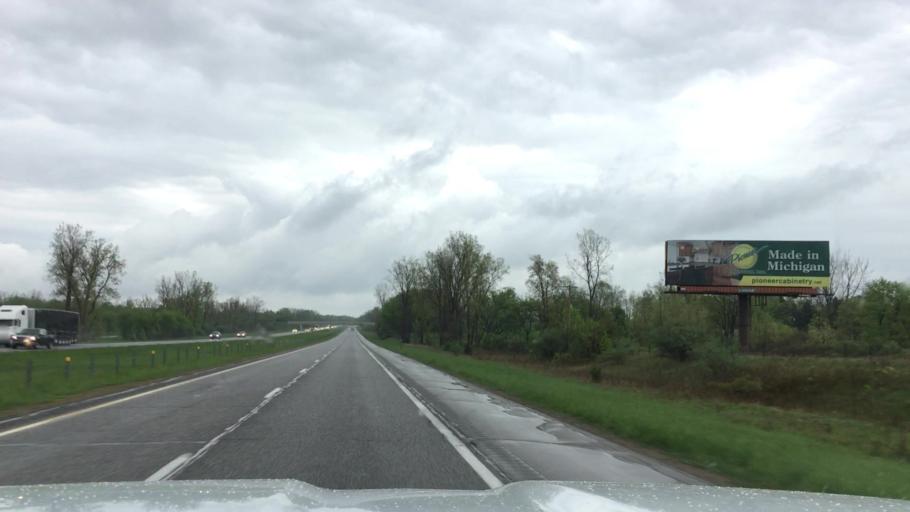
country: US
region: Michigan
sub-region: Shiawassee County
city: Perry
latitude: 42.8481
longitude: -84.1874
